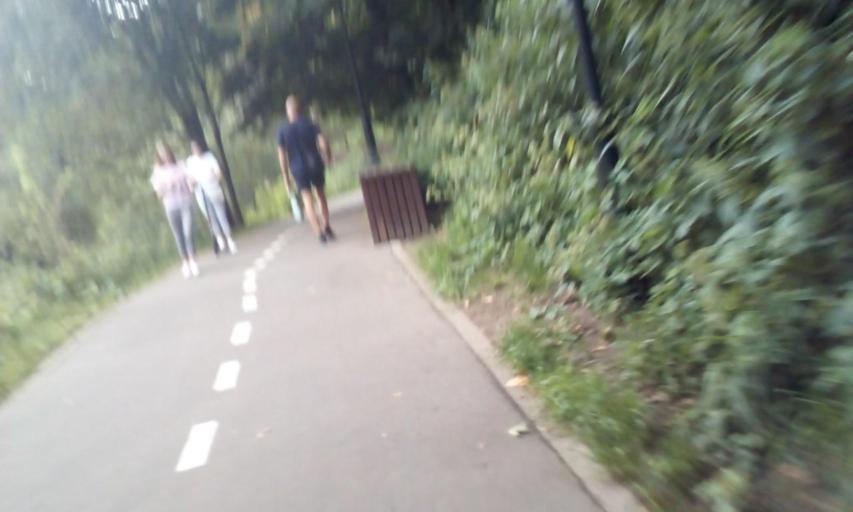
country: RU
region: Moscow
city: Sviblovo
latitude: 55.8537
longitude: 37.6333
